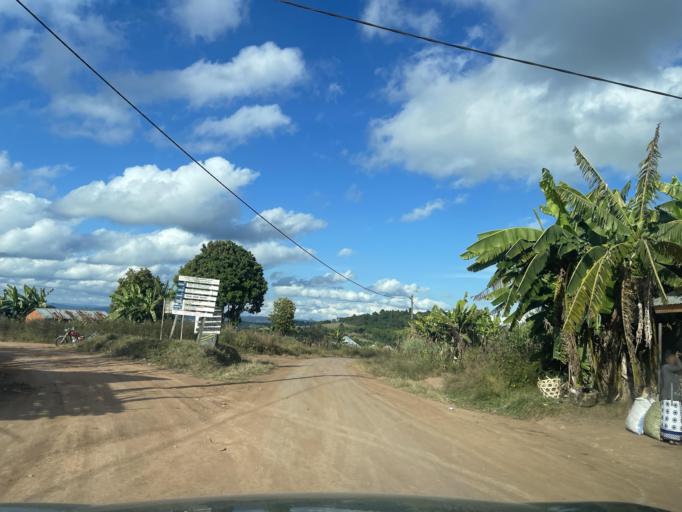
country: TZ
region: Morogoro
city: Mlimba
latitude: -8.4971
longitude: 35.5904
